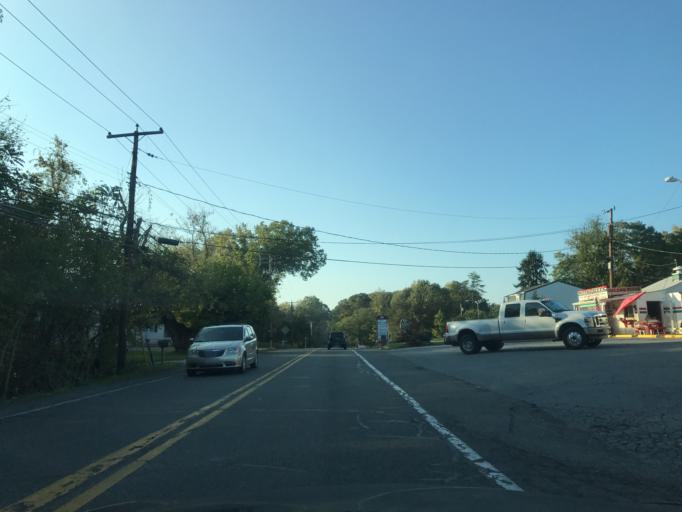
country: US
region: Maryland
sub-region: Anne Arundel County
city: Crownsville
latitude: 39.0532
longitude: -76.6190
